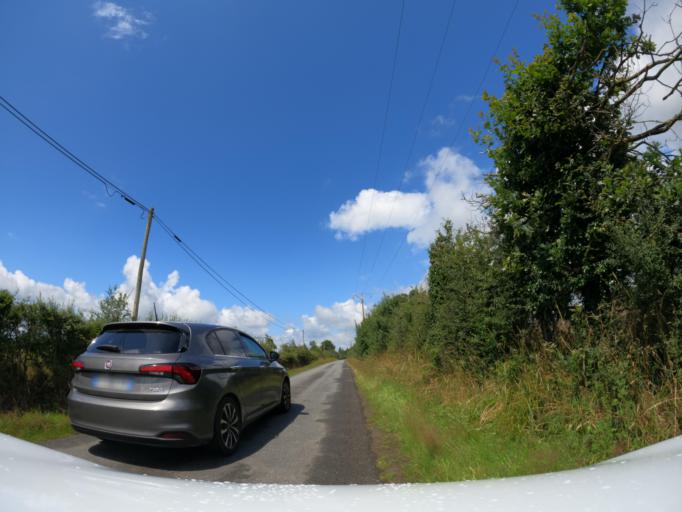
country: FR
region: Pays de la Loire
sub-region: Departement de la Loire-Atlantique
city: Saint-Mars-du-Desert
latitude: 47.3895
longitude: -1.4025
